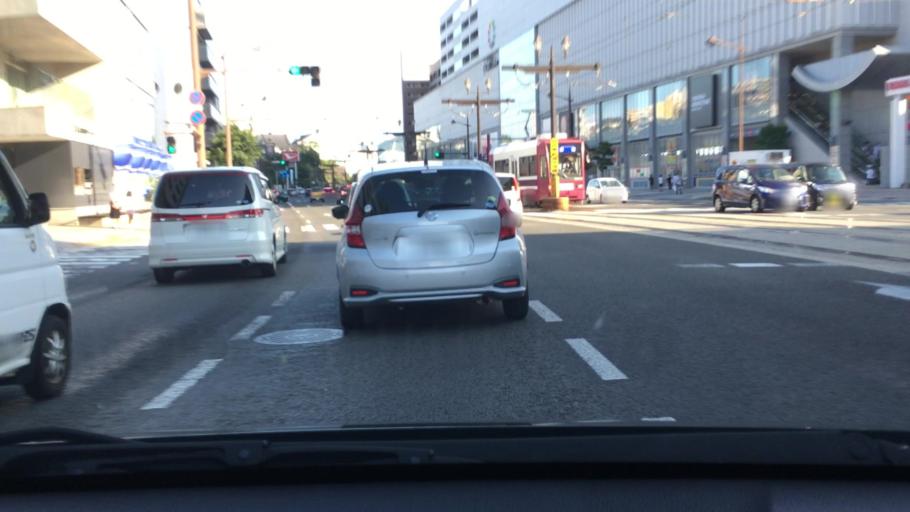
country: JP
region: Nagasaki
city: Nagasaki-shi
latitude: 32.7640
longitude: 129.8647
